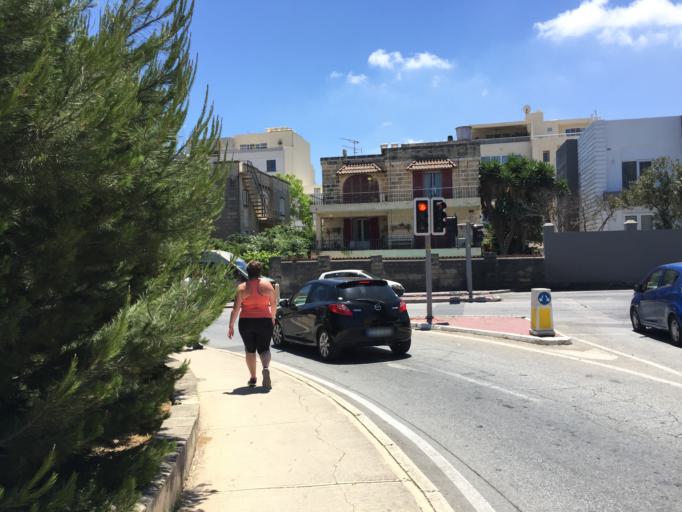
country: MT
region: Is-Swieqi
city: Swieqi
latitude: 35.9235
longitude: 14.4813
